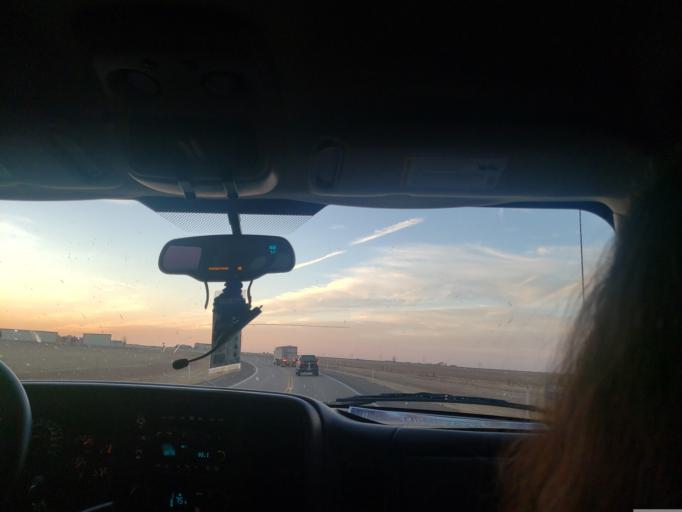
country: US
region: Kansas
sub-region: Seward County
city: Liberal
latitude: 37.0700
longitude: -100.9084
